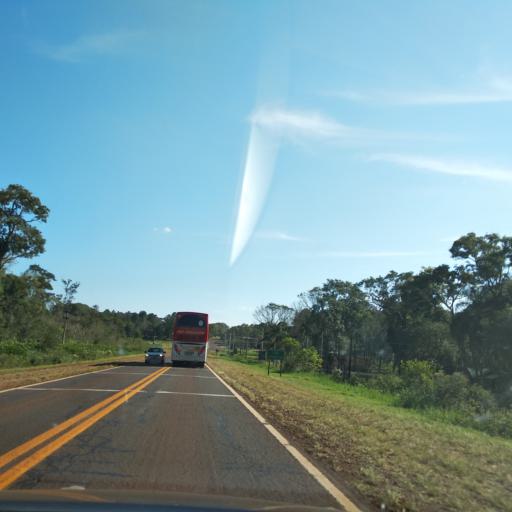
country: AR
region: Misiones
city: Santo Pipo
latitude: -27.1404
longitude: -55.4026
